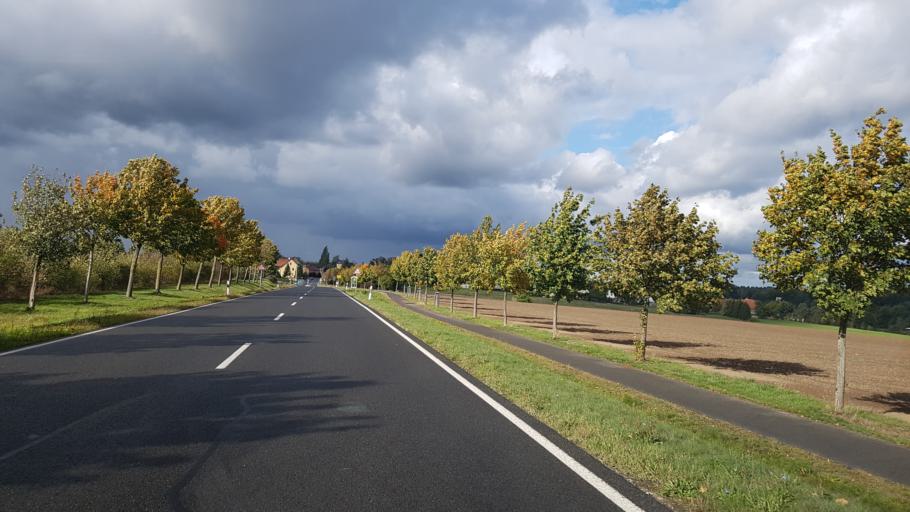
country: DE
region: Saxony
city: Dahlen
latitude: 51.3914
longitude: 12.9879
